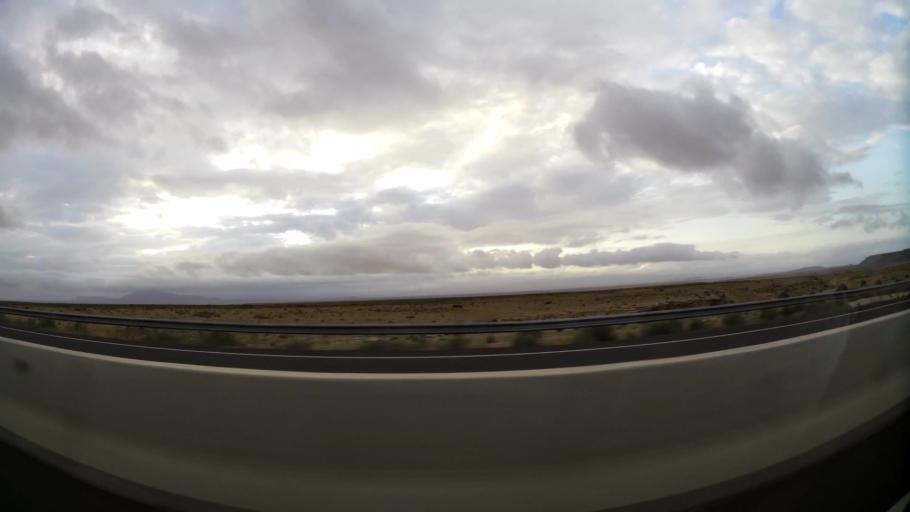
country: MA
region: Oriental
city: Taourirt
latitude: 34.4294
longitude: -3.0975
